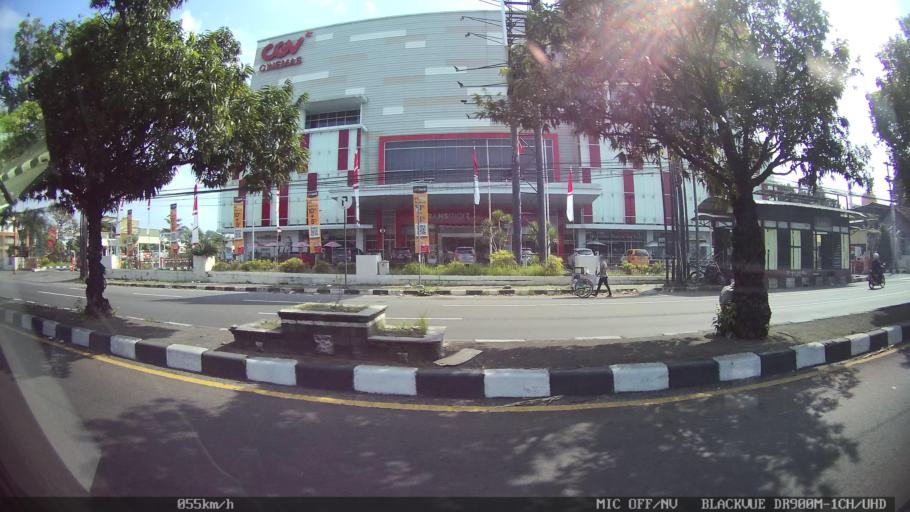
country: ID
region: Daerah Istimewa Yogyakarta
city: Depok
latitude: -7.7831
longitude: 110.4204
